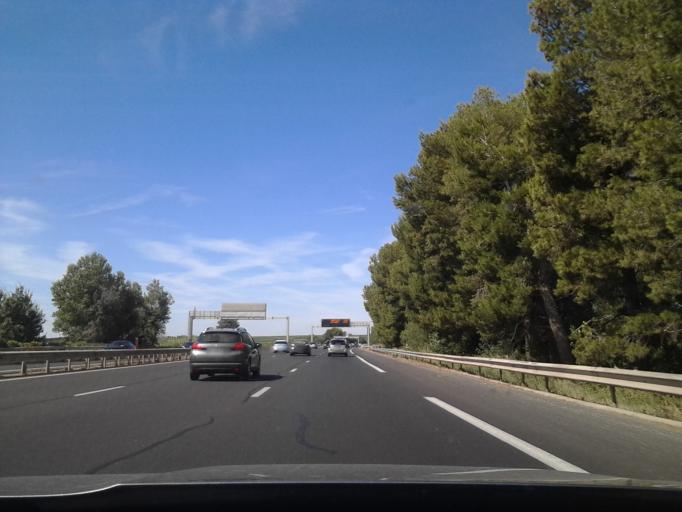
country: FR
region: Languedoc-Roussillon
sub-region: Departement de l'Herault
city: Sauvian
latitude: 43.3118
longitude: 3.2526
